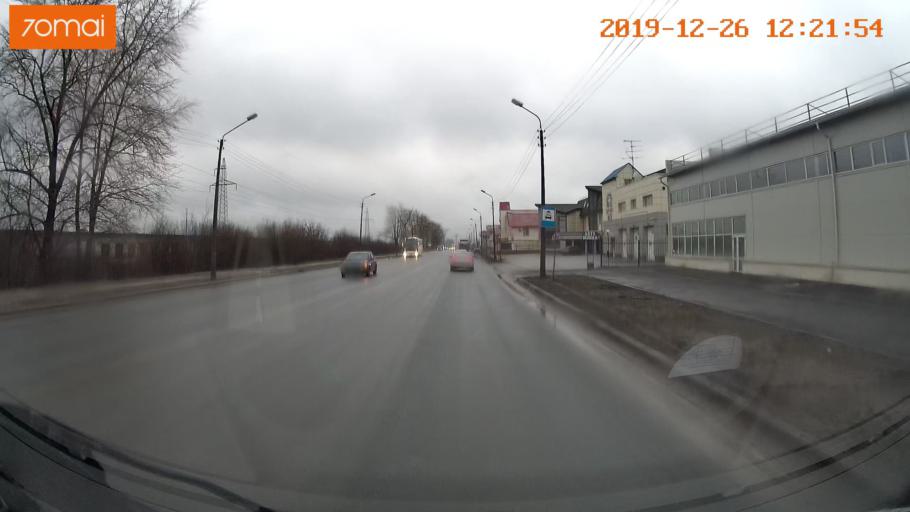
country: RU
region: Vologda
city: Cherepovets
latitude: 59.1512
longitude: 37.9377
